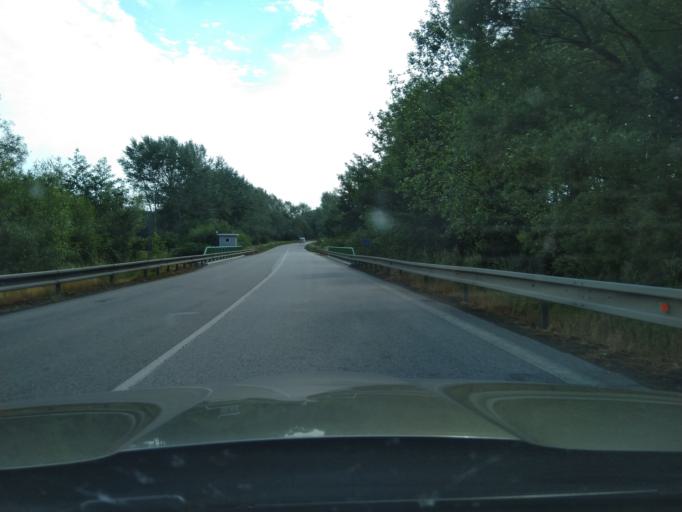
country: CZ
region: Jihocesky
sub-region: Okres Prachatice
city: Strunkovice nad Blanici
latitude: 49.0560
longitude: 14.0780
